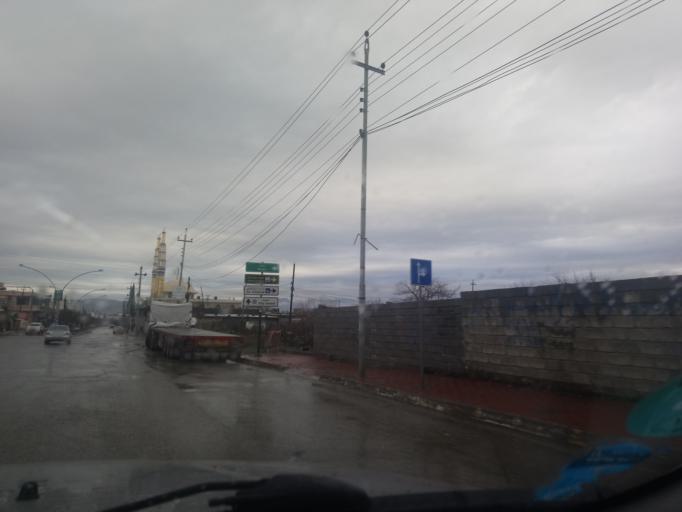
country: IQ
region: As Sulaymaniyah
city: Qeladize
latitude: 36.1775
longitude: 45.1454
